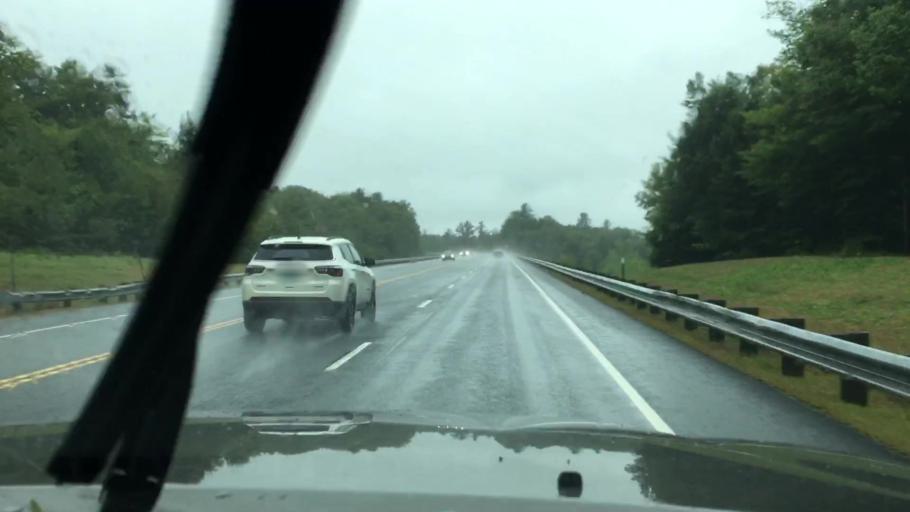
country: US
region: New Hampshire
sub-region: Cheshire County
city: Harrisville
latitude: 43.0165
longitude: -72.1361
